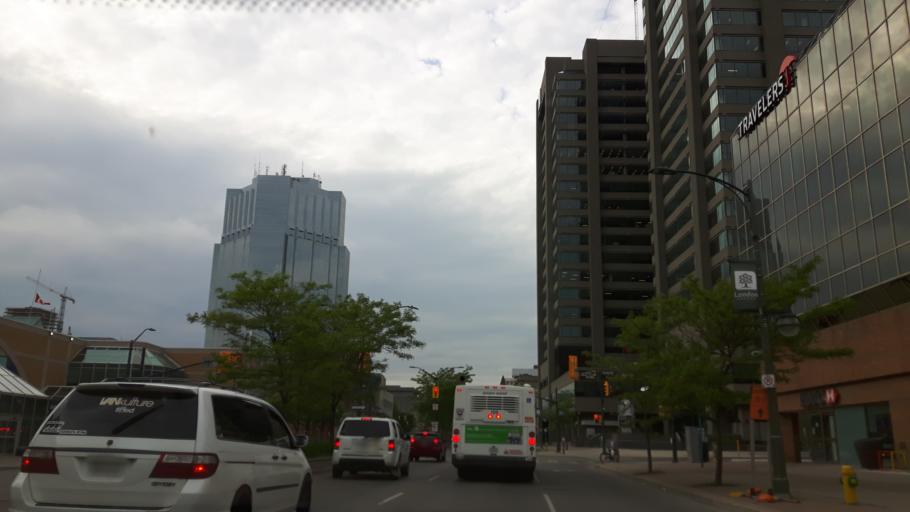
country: CA
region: Ontario
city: London
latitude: 42.9832
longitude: -81.2444
